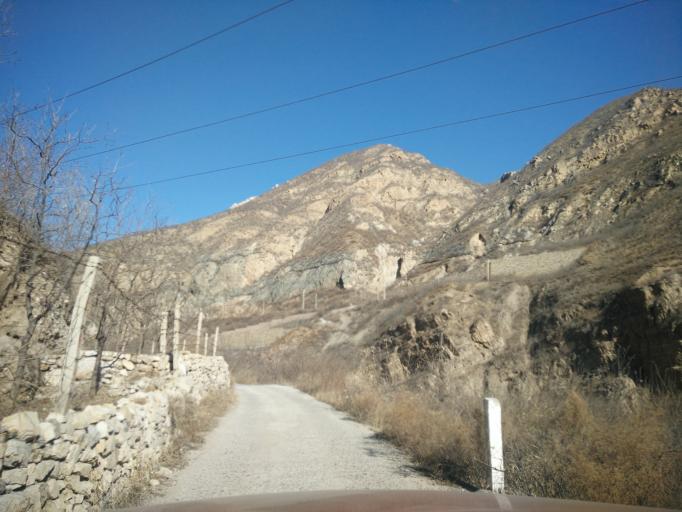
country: CN
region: Beijing
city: Yanjiatai
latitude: 40.1670
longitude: 115.6415
